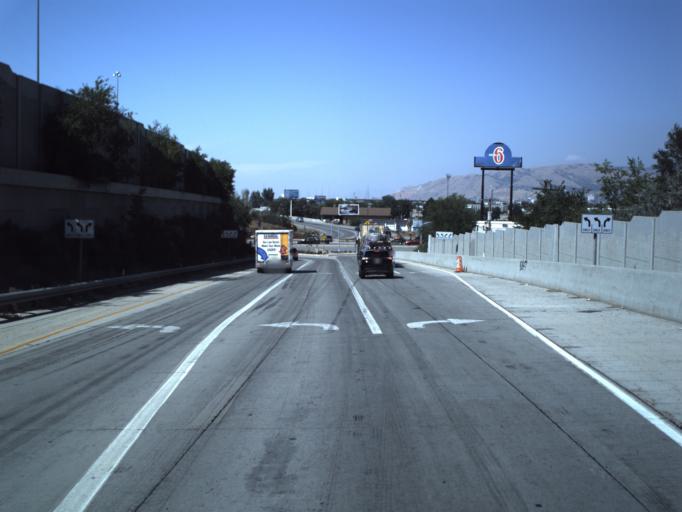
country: US
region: Utah
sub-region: Salt Lake County
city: Centerfield
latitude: 40.6982
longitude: -111.9013
